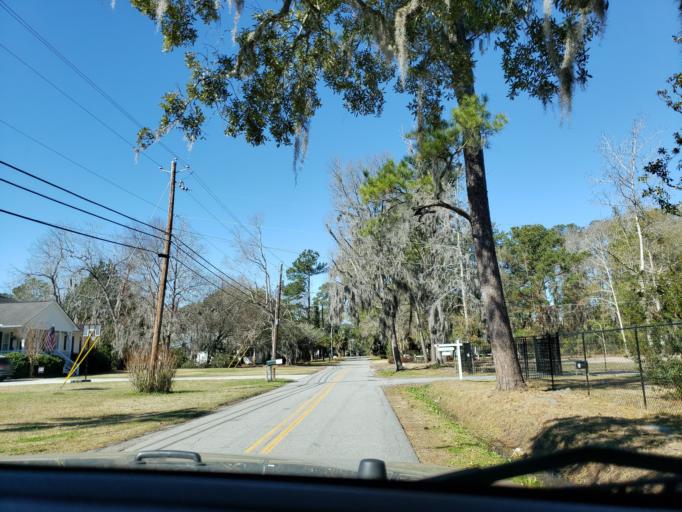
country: US
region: Georgia
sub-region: Chatham County
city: Whitemarsh Island
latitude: 32.0409
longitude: -80.9922
